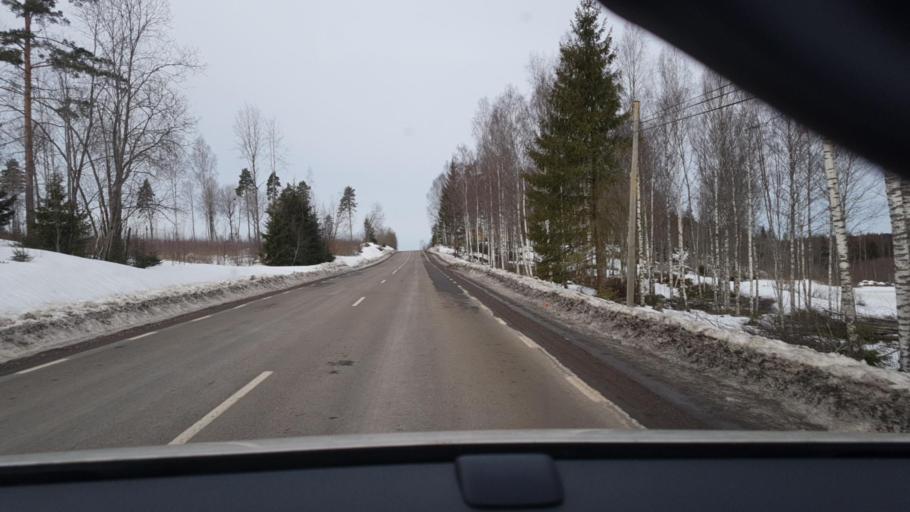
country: SE
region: Vaermland
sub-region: Eda Kommun
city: Amotfors
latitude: 59.7486
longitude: 12.3710
